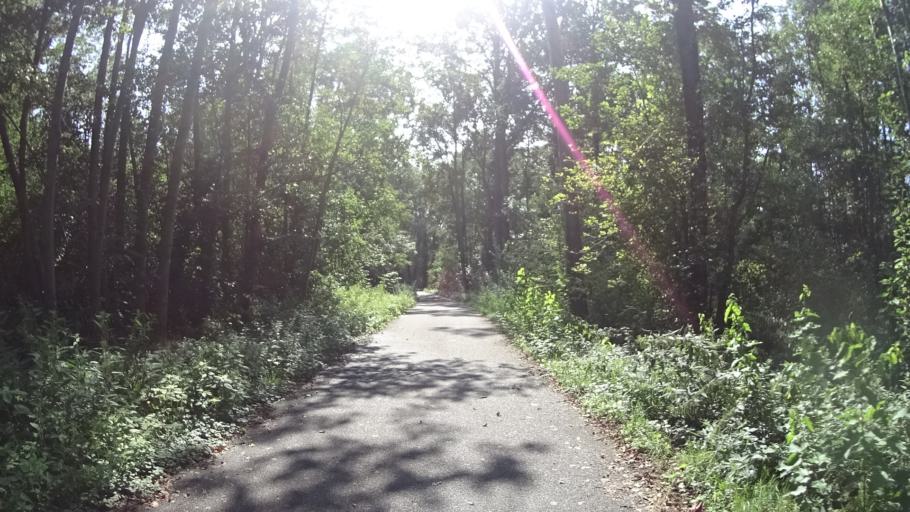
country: DE
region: Brandenburg
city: Burg
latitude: 51.8256
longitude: 14.1503
